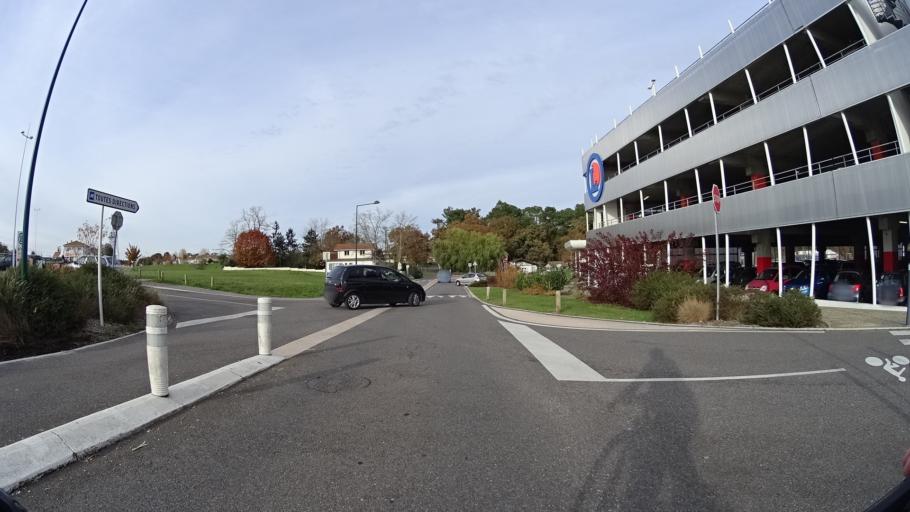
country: FR
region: Aquitaine
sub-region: Departement des Landes
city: Saint-Paul-les-Dax
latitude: 43.7318
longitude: -1.0449
